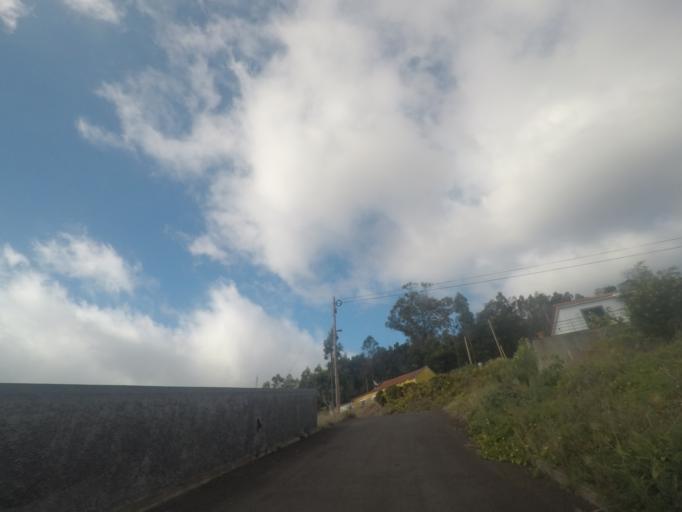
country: PT
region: Madeira
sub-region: Santa Cruz
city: Camacha
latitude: 32.6639
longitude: -16.8673
